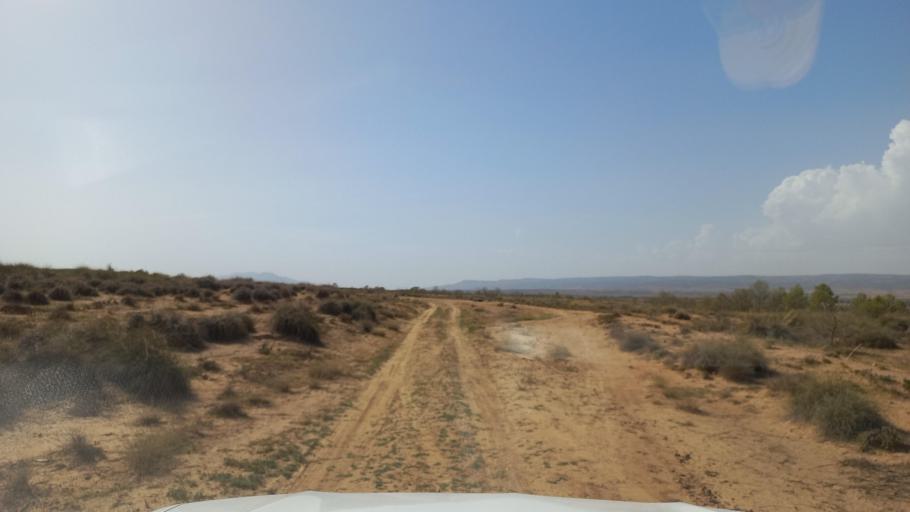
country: TN
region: Al Qasrayn
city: Kasserine
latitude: 35.2148
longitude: 9.0141
